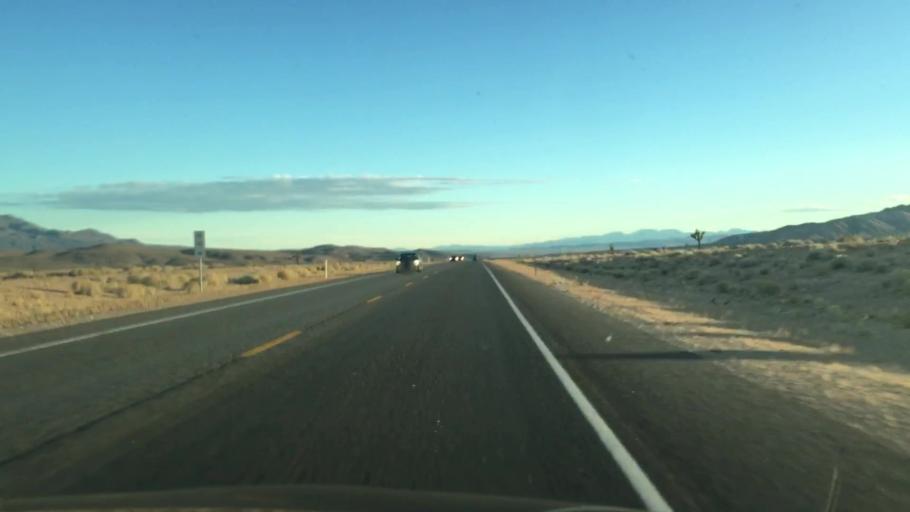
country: US
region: Nevada
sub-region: Esmeralda County
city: Goldfield
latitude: 37.5986
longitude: -117.2119
